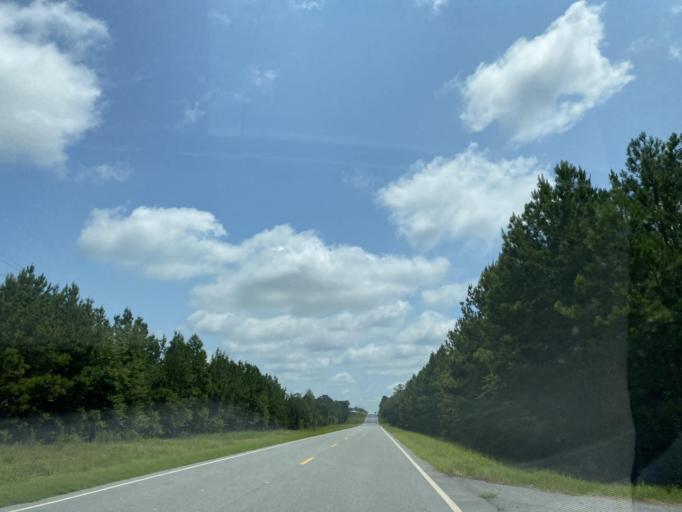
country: US
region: Georgia
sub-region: Telfair County
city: Helena
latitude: 32.0322
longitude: -82.9984
